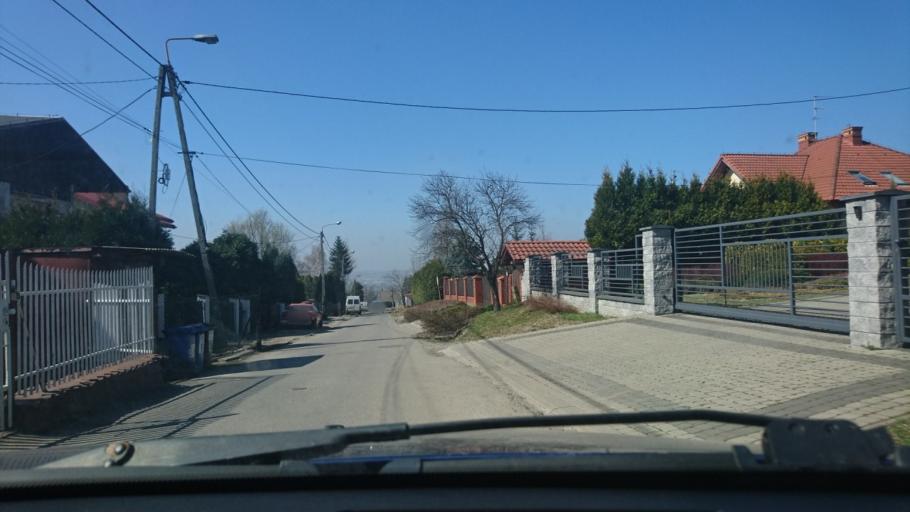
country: PL
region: Silesian Voivodeship
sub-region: Bielsko-Biala
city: Bielsko-Biala
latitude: 49.8449
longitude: 19.0785
